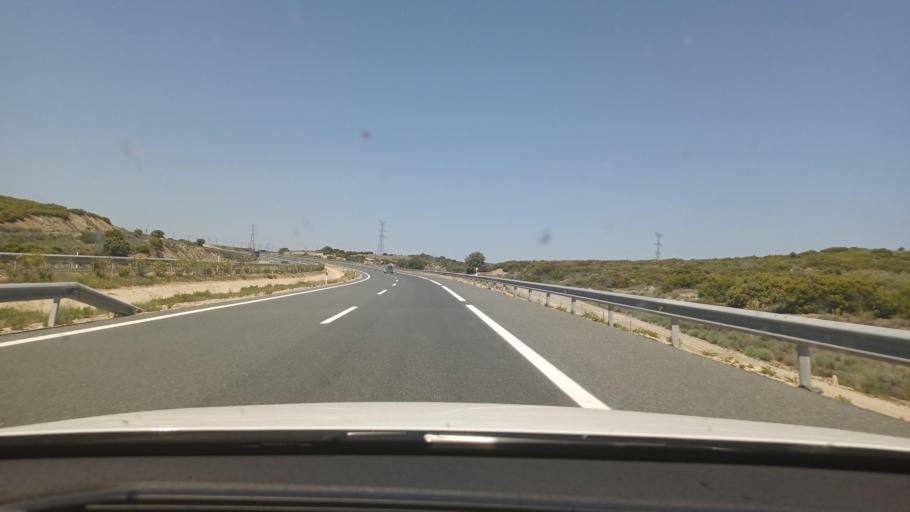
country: ES
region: Castille-La Mancha
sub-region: Provincia de Albacete
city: Alpera
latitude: 38.8805
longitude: -1.2468
